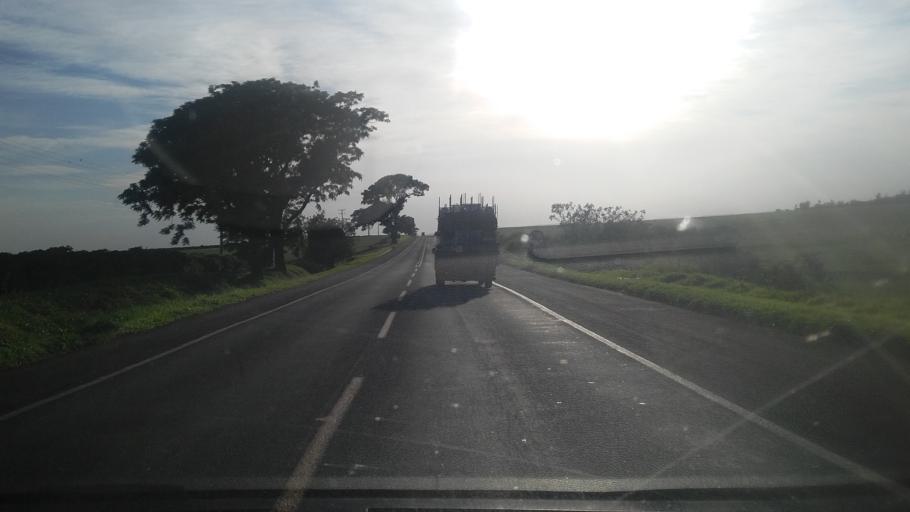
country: BR
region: Parana
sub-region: Bandeirantes
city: Bandeirantes
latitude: -23.1459
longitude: -50.5699
